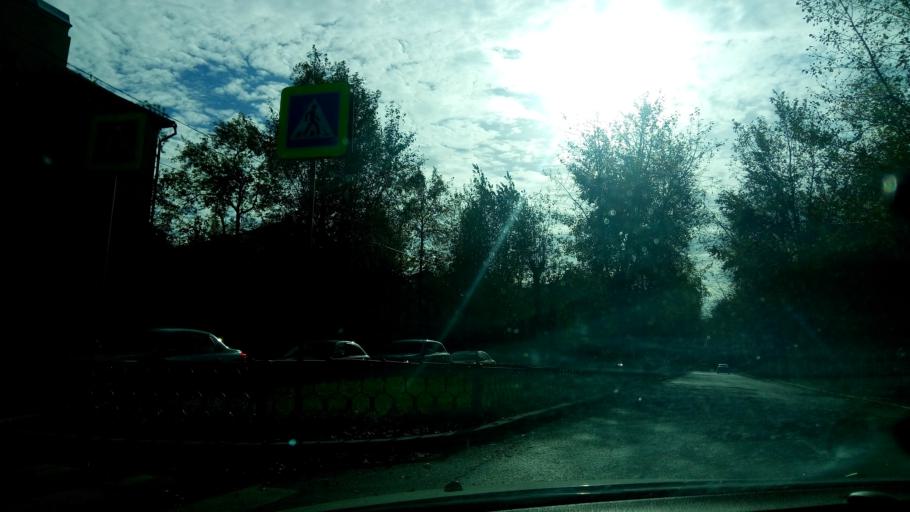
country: RU
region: Sverdlovsk
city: Yekaterinburg
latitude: 56.8896
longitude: 60.6209
